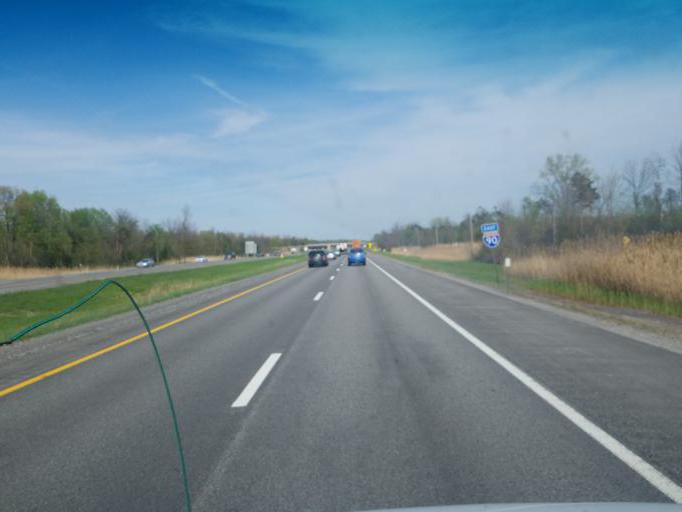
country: US
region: New York
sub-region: Onondaga County
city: Minoa
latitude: 43.0947
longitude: -76.0386
